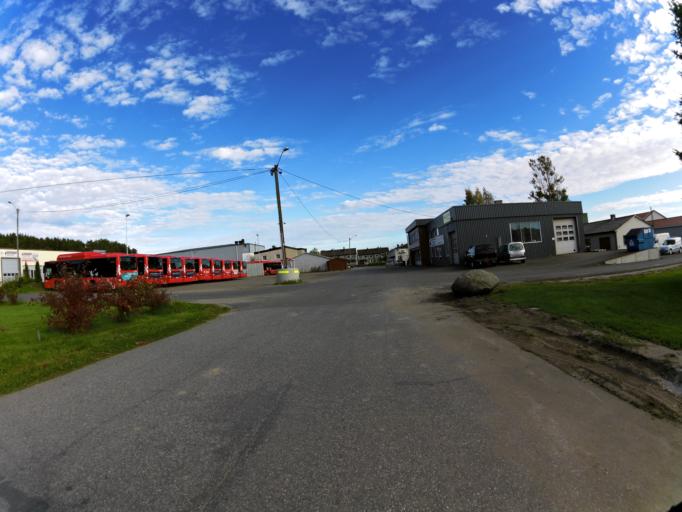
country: NO
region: Ostfold
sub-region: Sarpsborg
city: Sarpsborg
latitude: 59.2905
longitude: 11.0869
